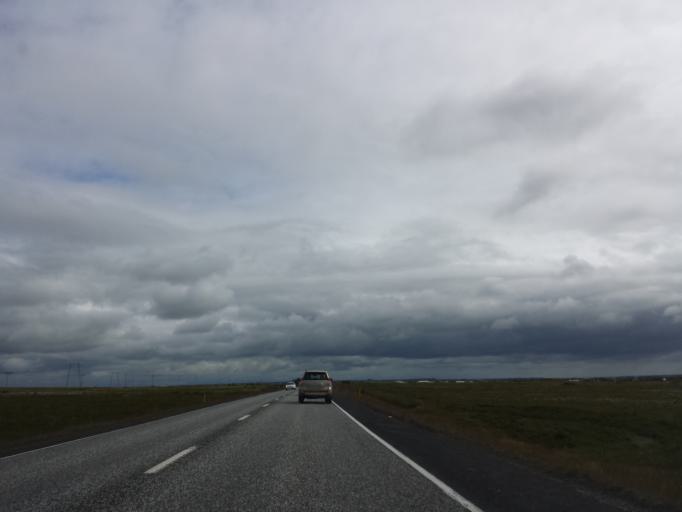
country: IS
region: South
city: Selfoss
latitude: 63.9548
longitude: -21.0437
